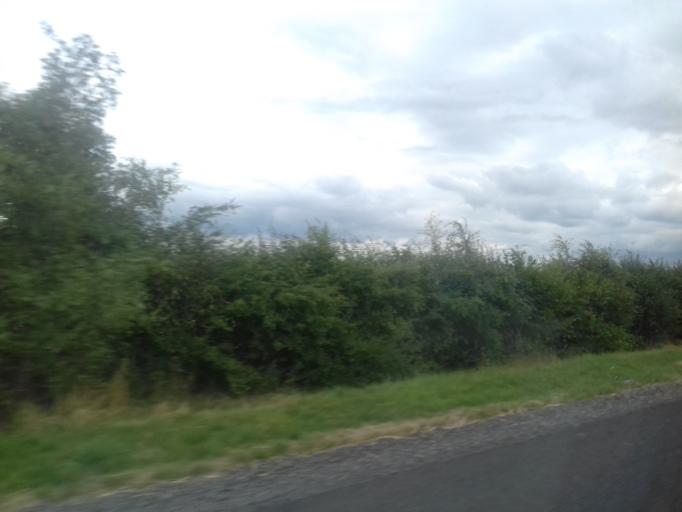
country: IE
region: Leinster
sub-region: County Carlow
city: Bagenalstown
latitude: 52.7229
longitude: -7.0076
